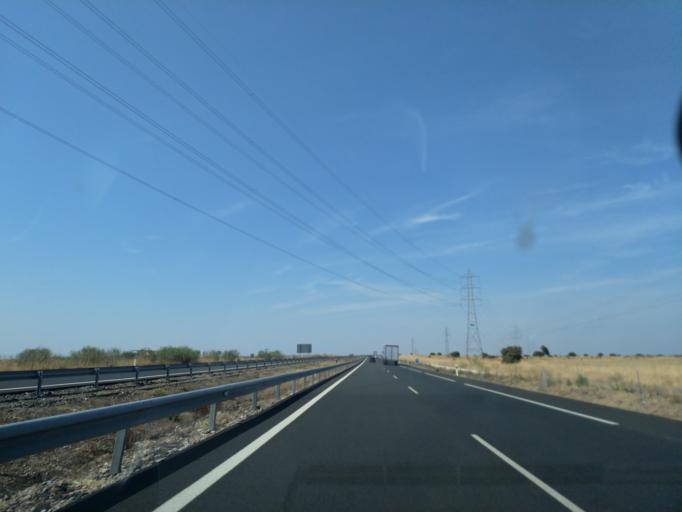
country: ES
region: Castille-La Mancha
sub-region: Province of Toledo
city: Velada
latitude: 39.9357
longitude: -4.9870
